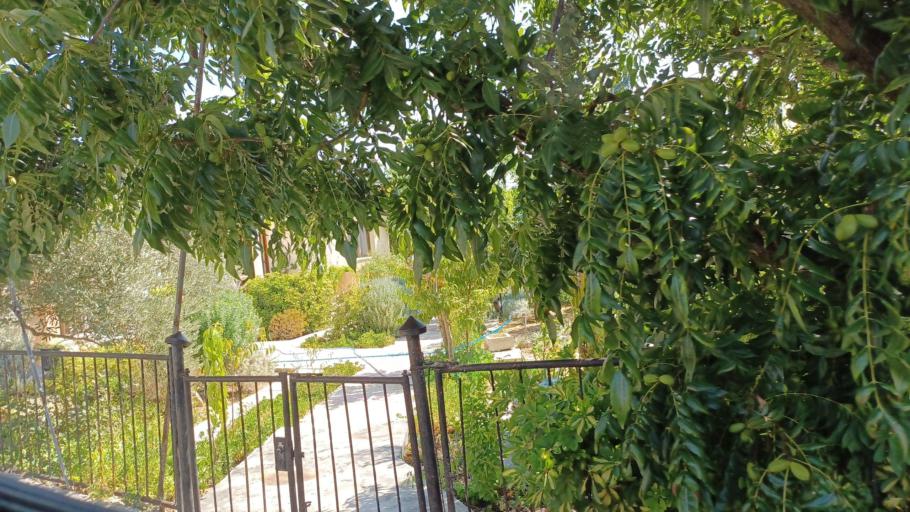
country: CY
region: Pafos
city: Tala
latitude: 34.9226
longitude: 32.4741
